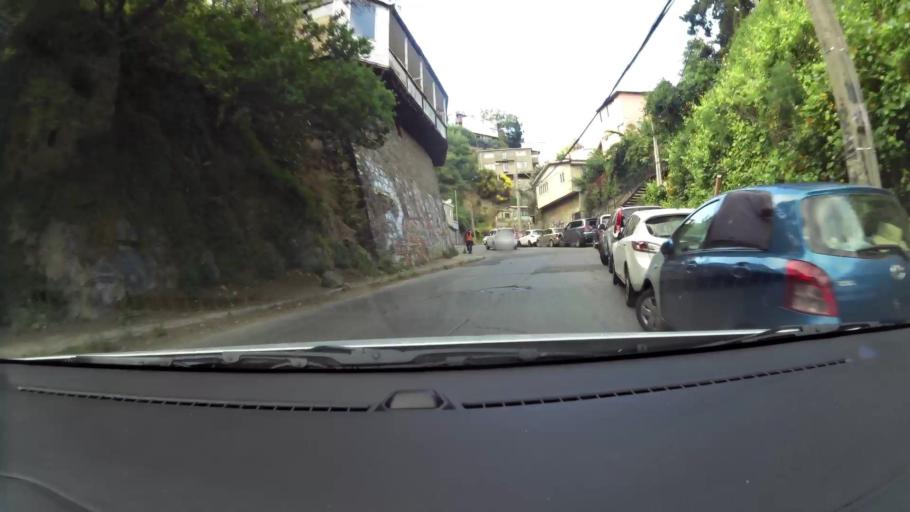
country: CL
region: Valparaiso
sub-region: Provincia de Valparaiso
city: Valparaiso
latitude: -33.0419
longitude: -71.6317
